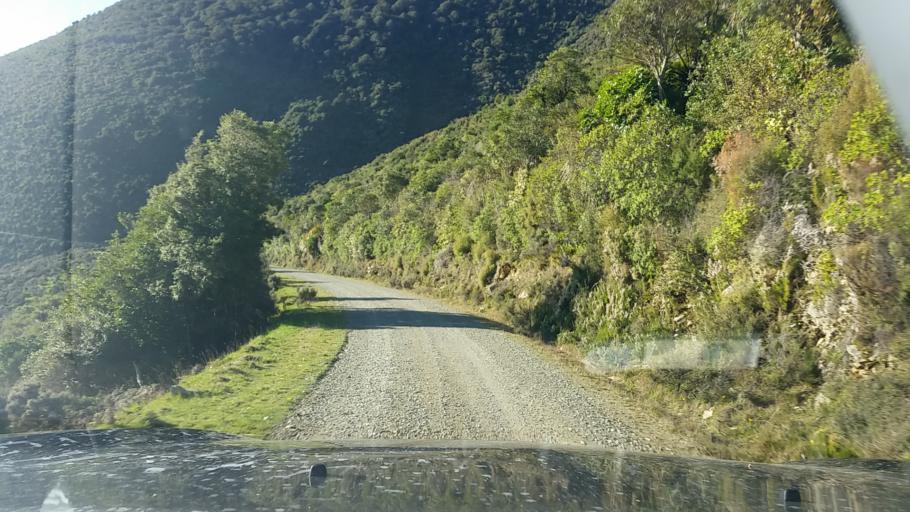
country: NZ
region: Marlborough
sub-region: Marlborough District
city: Picton
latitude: -41.0236
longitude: 174.1604
